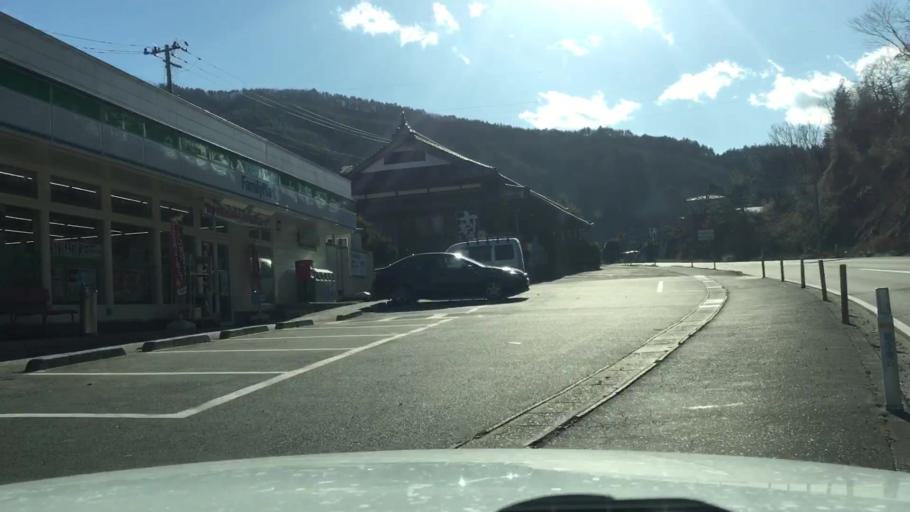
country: JP
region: Iwate
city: Miyako
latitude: 39.6189
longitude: 141.8005
